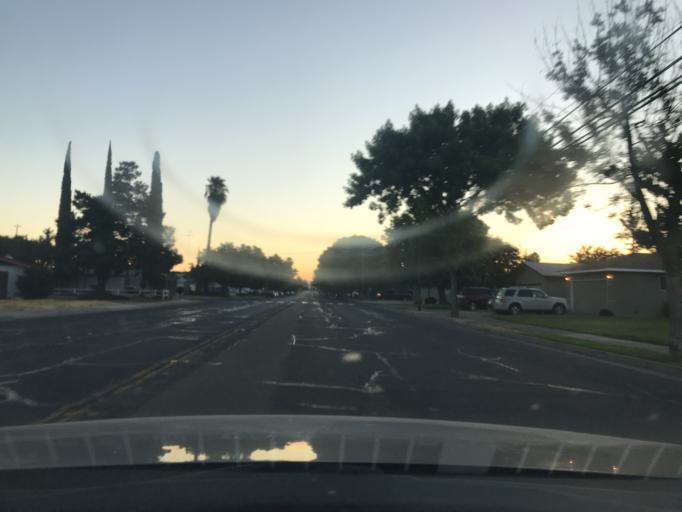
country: US
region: California
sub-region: Merced County
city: Atwater
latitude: 37.3546
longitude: -120.6007
